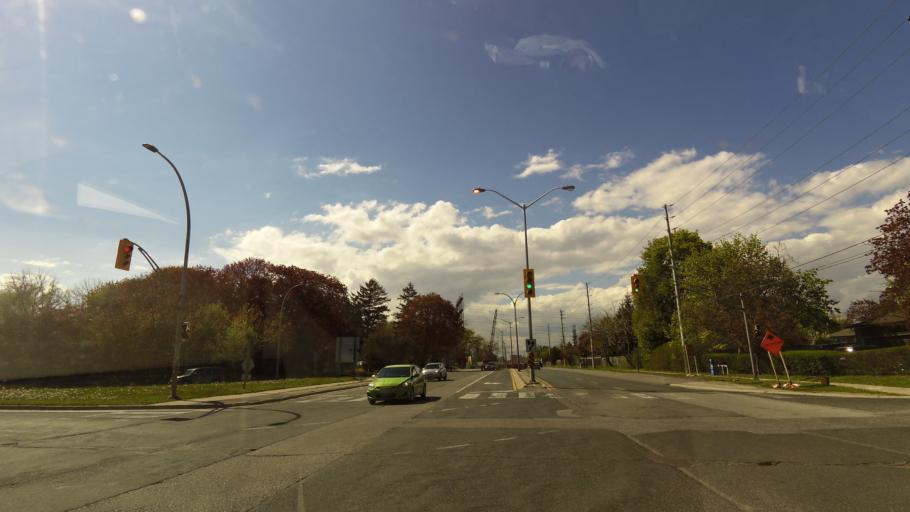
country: CA
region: Ontario
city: Etobicoke
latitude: 43.5996
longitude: -79.5700
